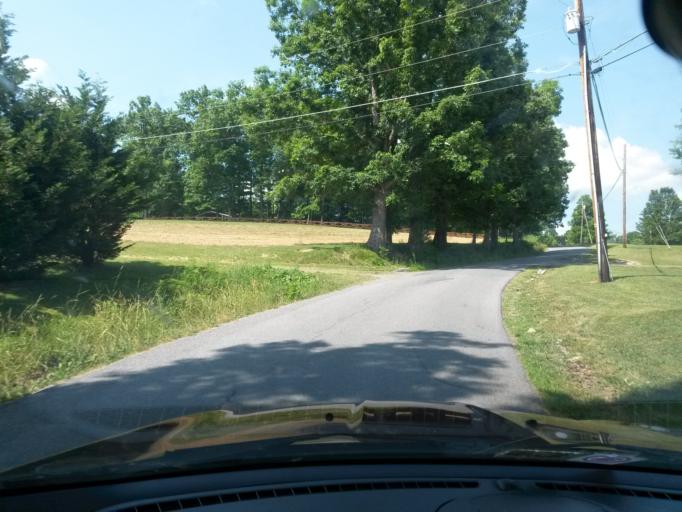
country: US
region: West Virginia
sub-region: Mercer County
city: Princeton
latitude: 37.3938
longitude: -81.1145
